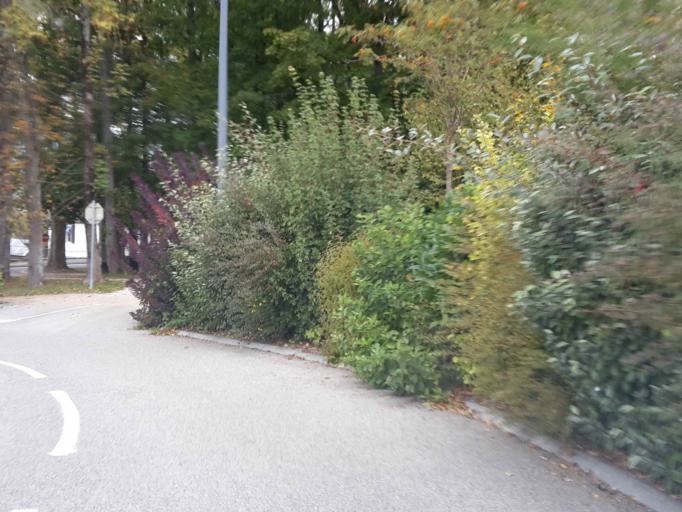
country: FR
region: Franche-Comte
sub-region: Departement du Doubs
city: Baume-les-Dames
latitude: 47.3468
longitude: 6.3617
